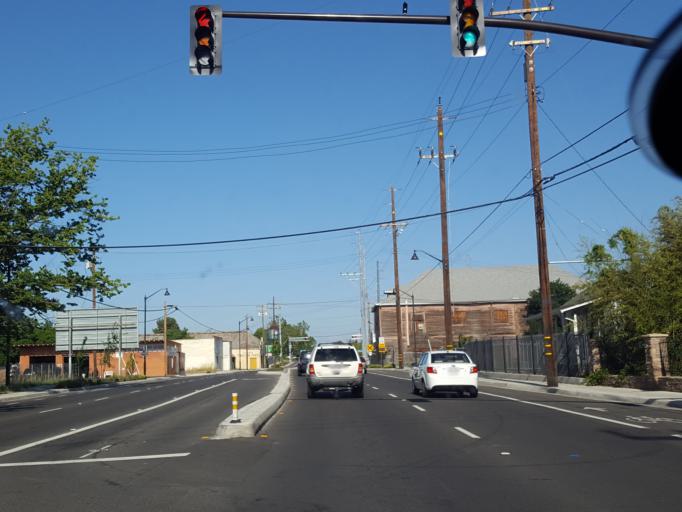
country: US
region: California
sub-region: Sacramento County
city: Florin
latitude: 38.4960
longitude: -121.3999
